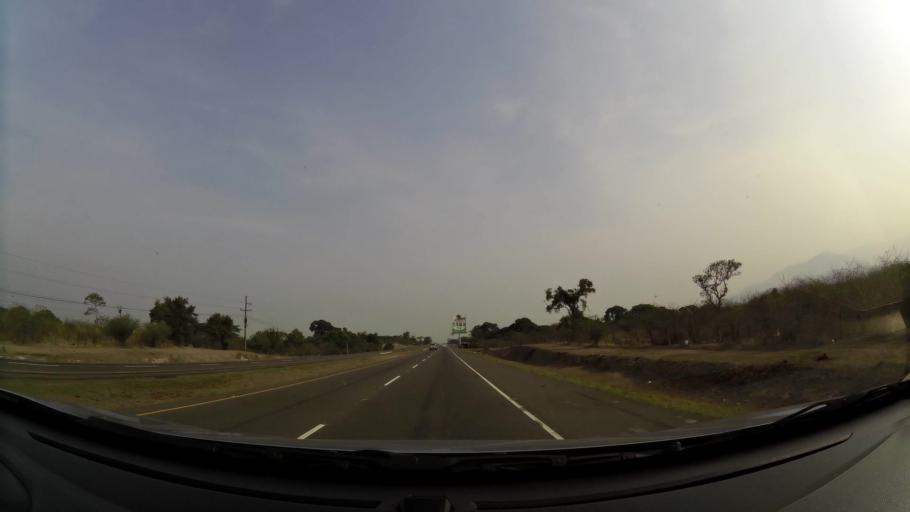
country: HN
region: La Paz
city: Yarumela
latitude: 14.3582
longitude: -87.5999
